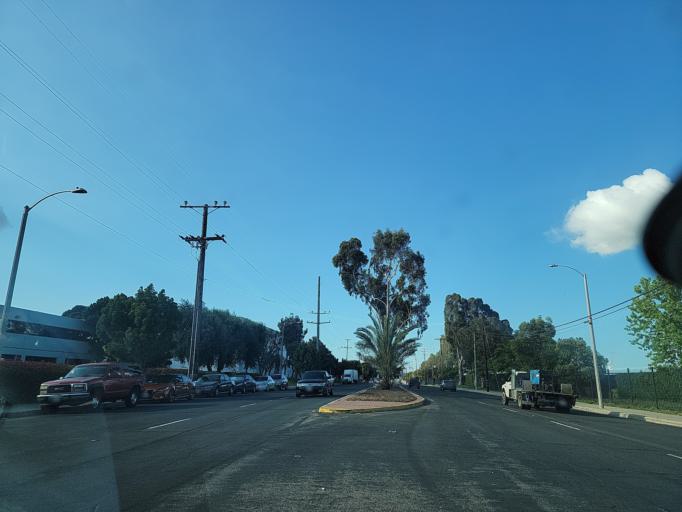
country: US
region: California
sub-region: Los Angeles County
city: West Carson
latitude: 33.8035
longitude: -118.2755
